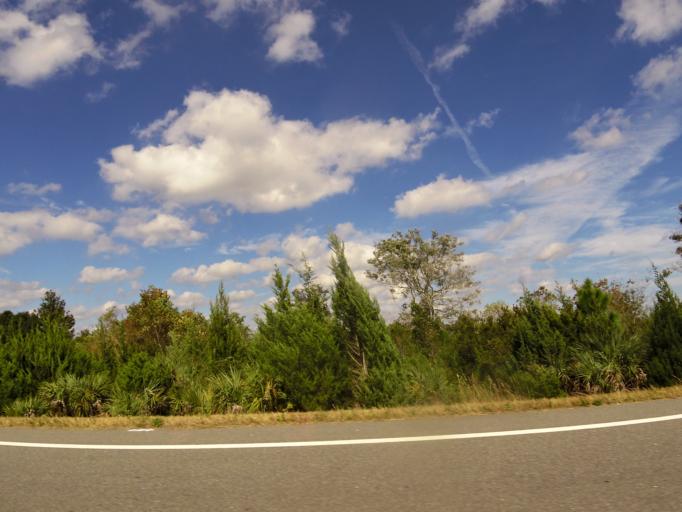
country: US
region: Florida
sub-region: Duval County
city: Jacksonville
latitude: 30.4187
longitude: -81.6349
